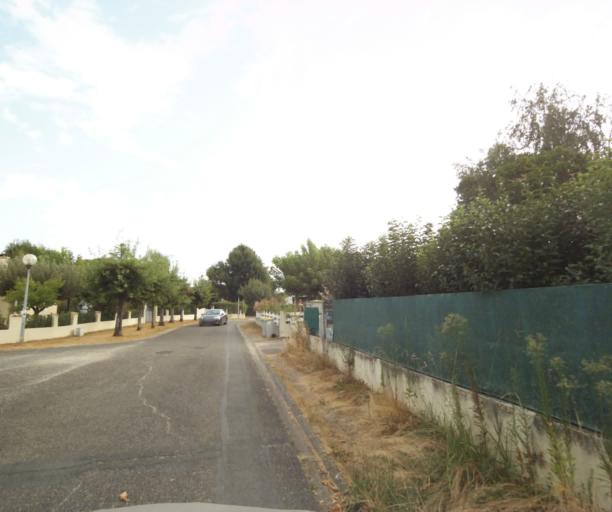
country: FR
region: Aquitaine
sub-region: Departement de la Gironde
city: Creon
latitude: 44.7696
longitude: -0.3449
